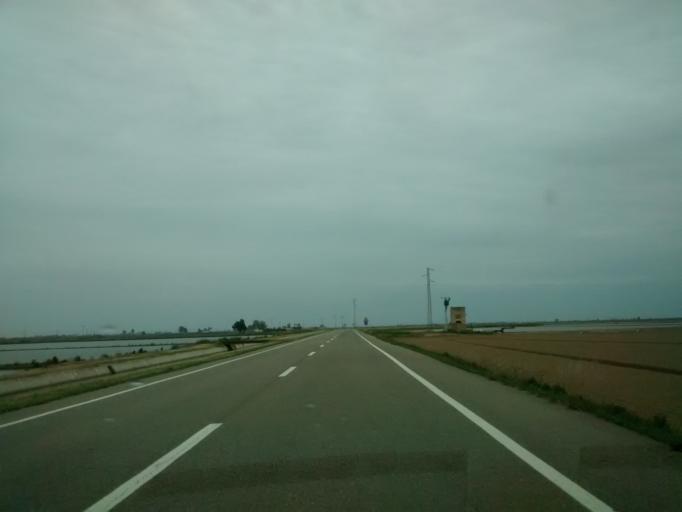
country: ES
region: Catalonia
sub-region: Provincia de Tarragona
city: Deltebre
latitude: 40.6959
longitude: 0.6805
